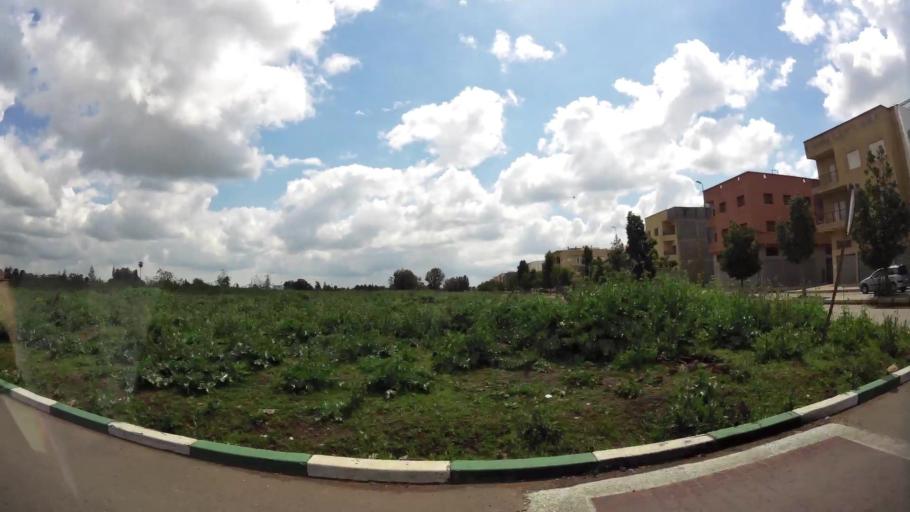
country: MA
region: Grand Casablanca
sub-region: Mediouna
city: Mediouna
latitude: 33.3882
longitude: -7.5426
